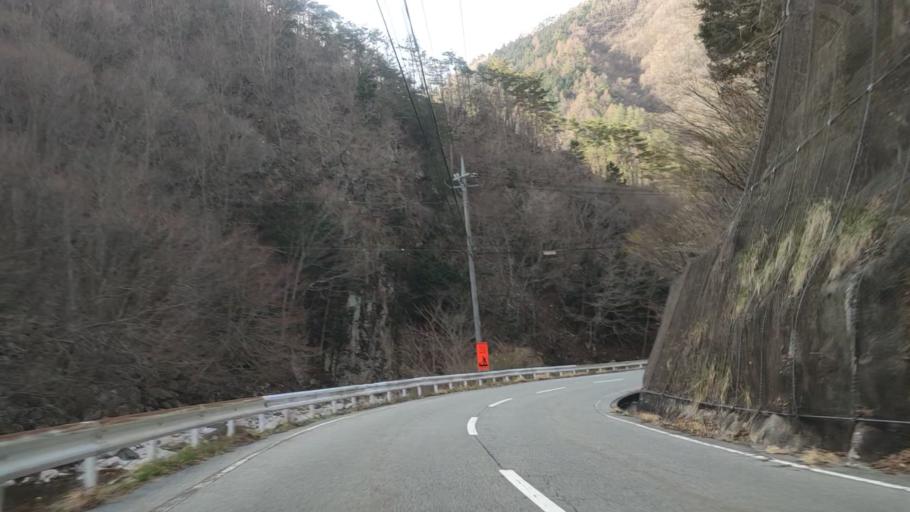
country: JP
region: Yamanashi
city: Fujikawaguchiko
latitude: 35.5418
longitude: 138.6407
